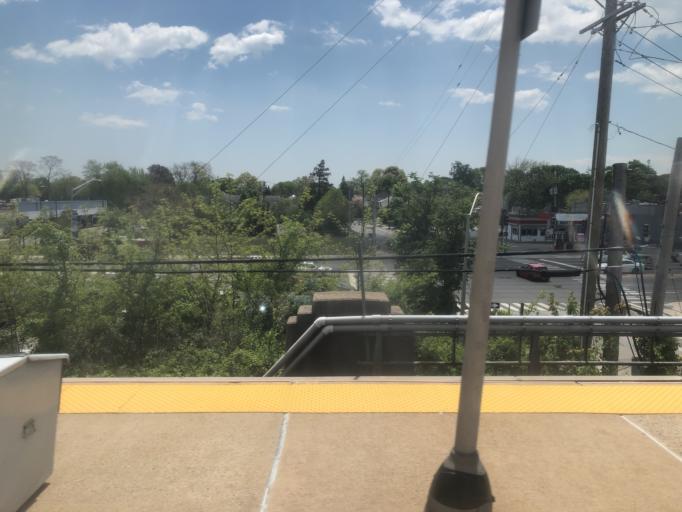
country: US
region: New York
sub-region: Nassau County
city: Baldwin
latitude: 40.6567
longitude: -73.6052
